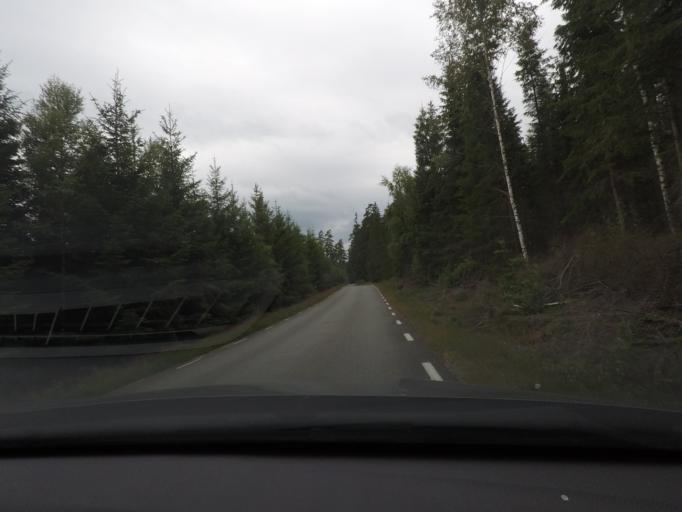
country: SE
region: Kronoberg
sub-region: Markaryds Kommun
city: Stromsnasbruk
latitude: 56.4235
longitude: 13.7372
